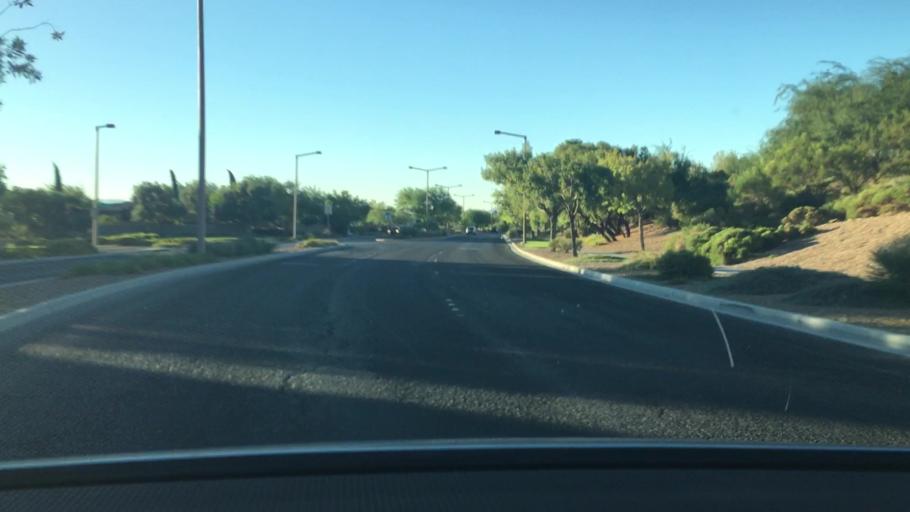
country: US
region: Nevada
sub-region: Clark County
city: Summerlin South
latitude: 36.1237
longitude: -115.3366
